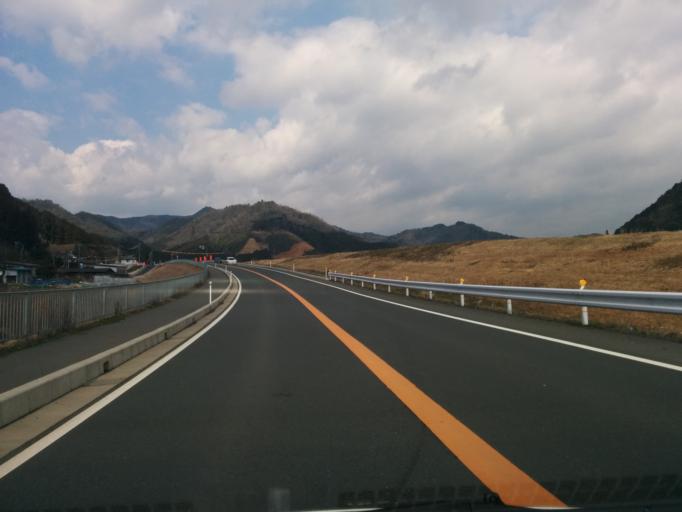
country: JP
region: Kyoto
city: Fukuchiyama
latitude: 35.3984
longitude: 135.1829
